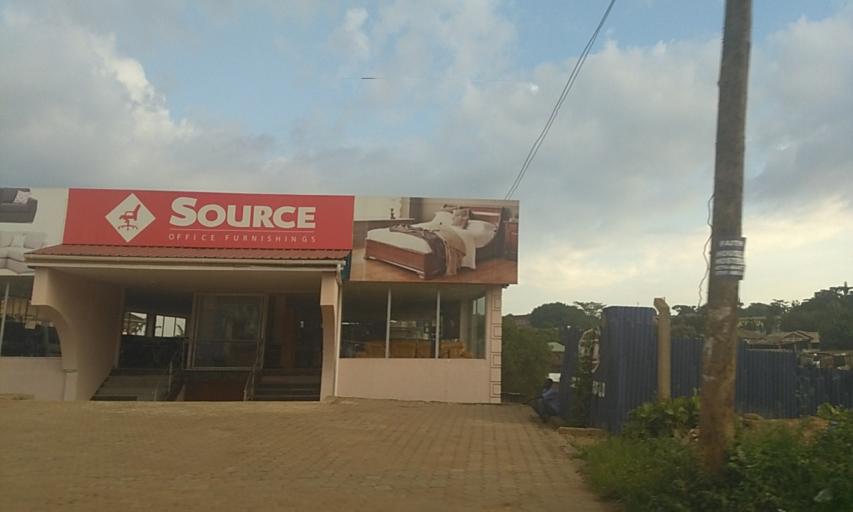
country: UG
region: Central Region
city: Kampala Central Division
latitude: 0.3088
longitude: 32.5635
